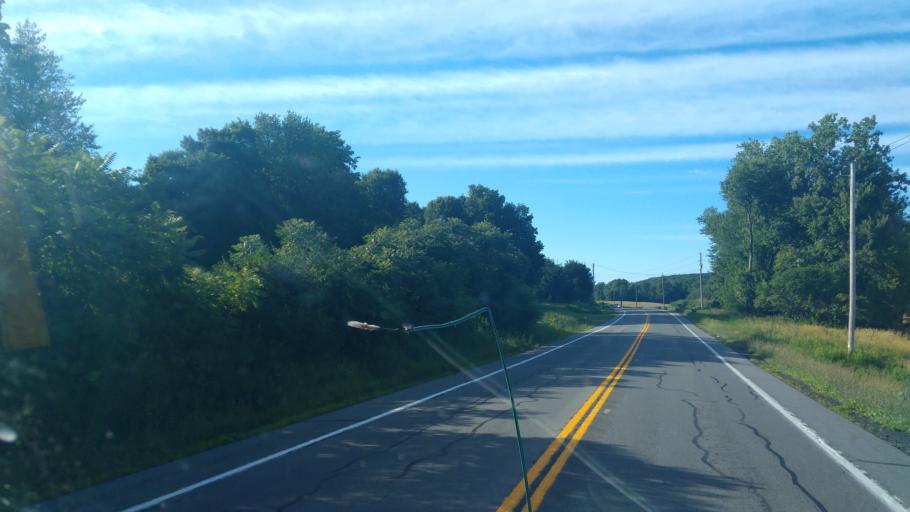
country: US
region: New York
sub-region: Wayne County
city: Lyons
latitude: 43.0963
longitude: -76.9843
